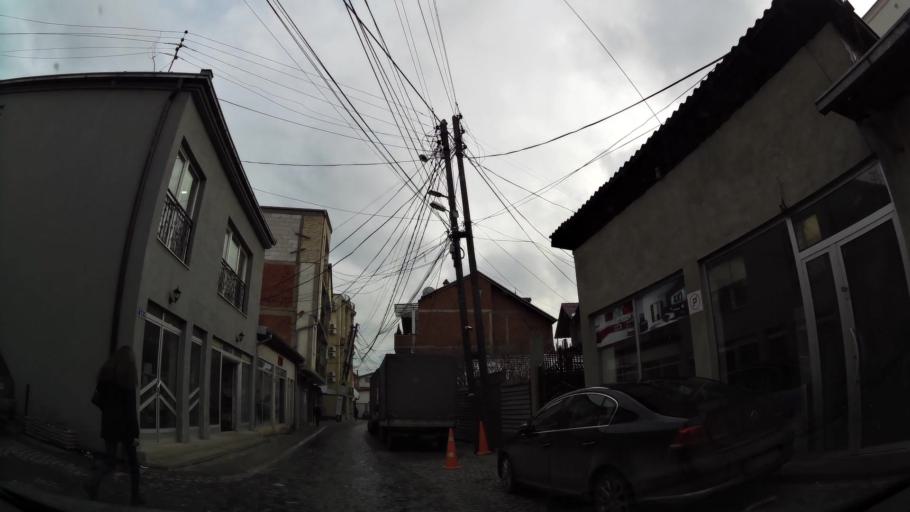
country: XK
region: Pristina
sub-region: Komuna e Prishtines
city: Pristina
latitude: 42.6704
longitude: 21.1644
